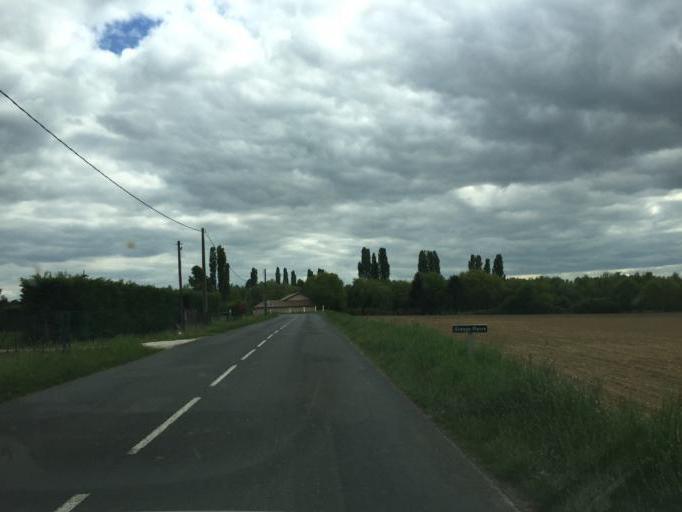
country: FR
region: Rhone-Alpes
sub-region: Departement de l'Ain
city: Saint-Andre-de-Corcy
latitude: 45.9473
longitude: 4.9387
